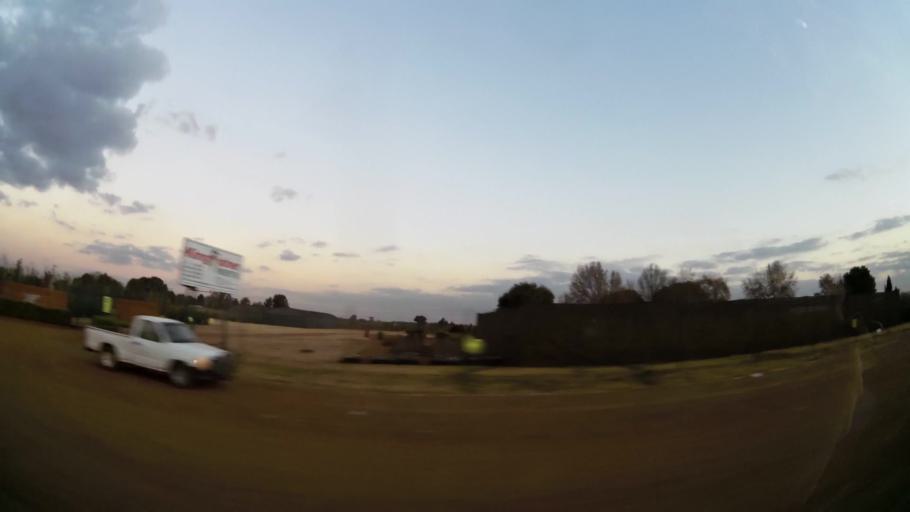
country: ZA
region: Gauteng
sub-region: West Rand District Municipality
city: Krugersdorp
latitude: -26.0715
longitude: 27.6663
